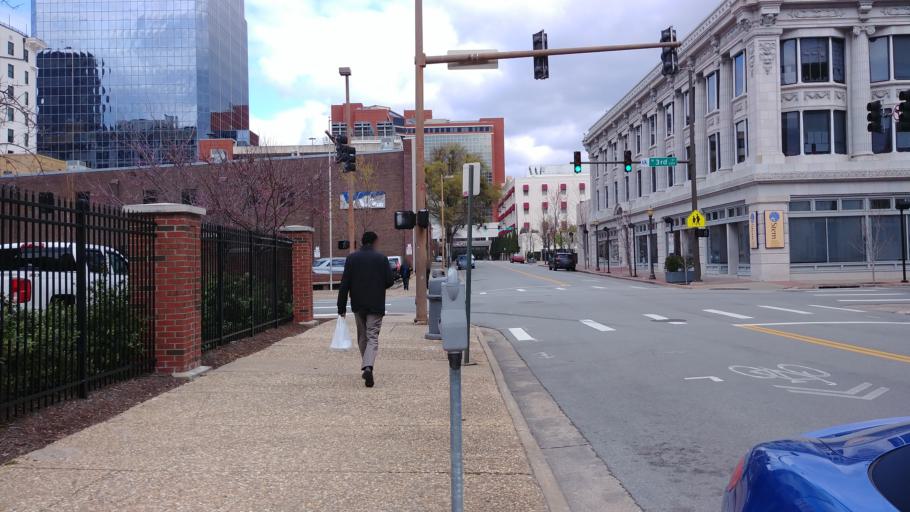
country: US
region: Arkansas
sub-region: Pulaski County
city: Little Rock
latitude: 34.7460
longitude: -92.2720
